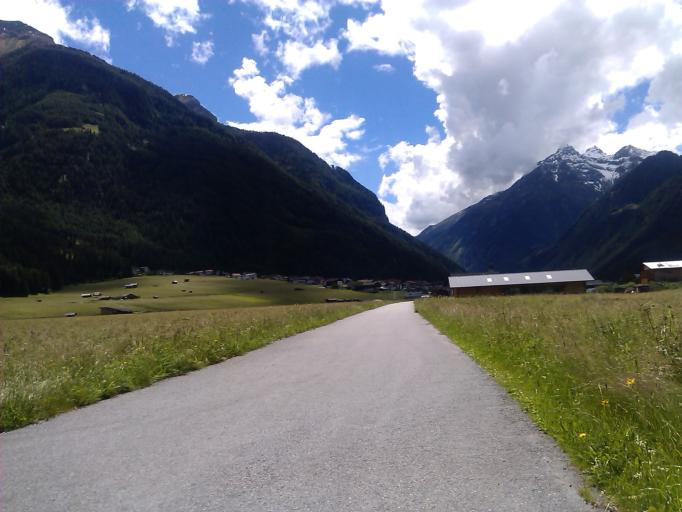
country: AT
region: Tyrol
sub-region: Politischer Bezirk Landeck
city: Pfunds
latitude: 46.9747
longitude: 10.5536
